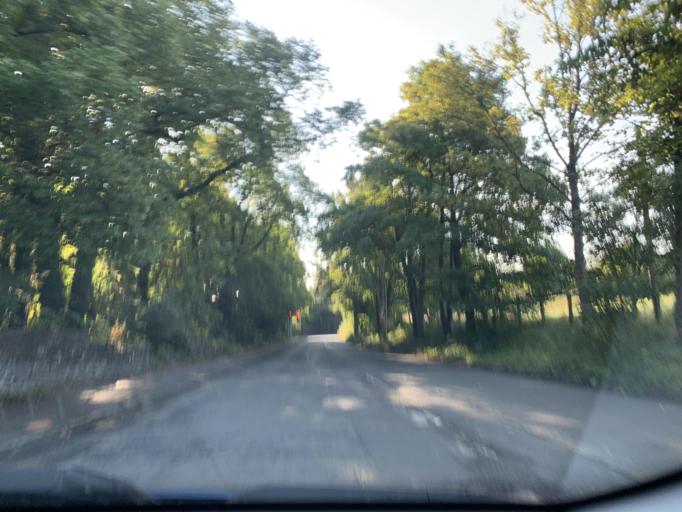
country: GB
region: Scotland
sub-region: East Renfrewshire
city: Giffnock
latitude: 55.8137
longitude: -4.3270
